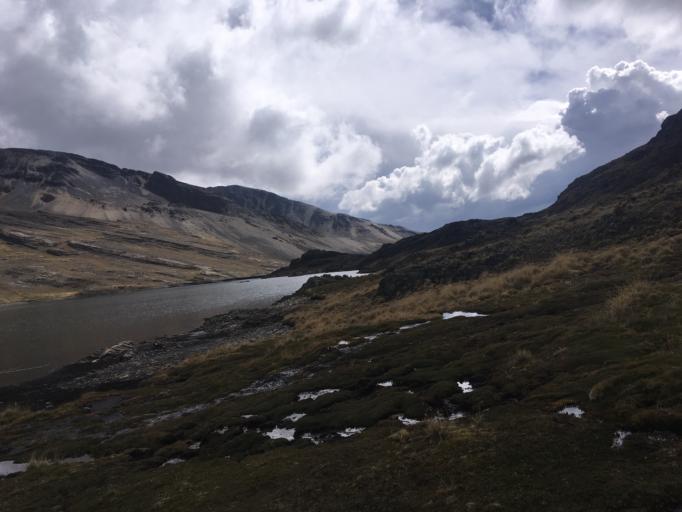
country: BO
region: La Paz
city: La Paz
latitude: -16.3931
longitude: -67.9669
